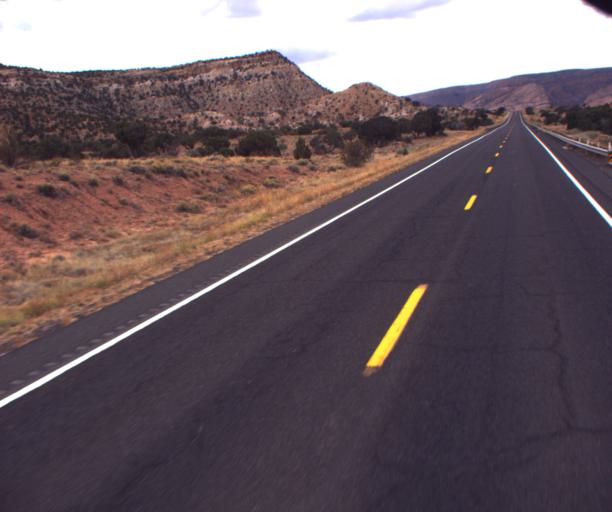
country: US
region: Arizona
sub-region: Navajo County
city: Kayenta
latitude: 36.6953
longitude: -110.3536
